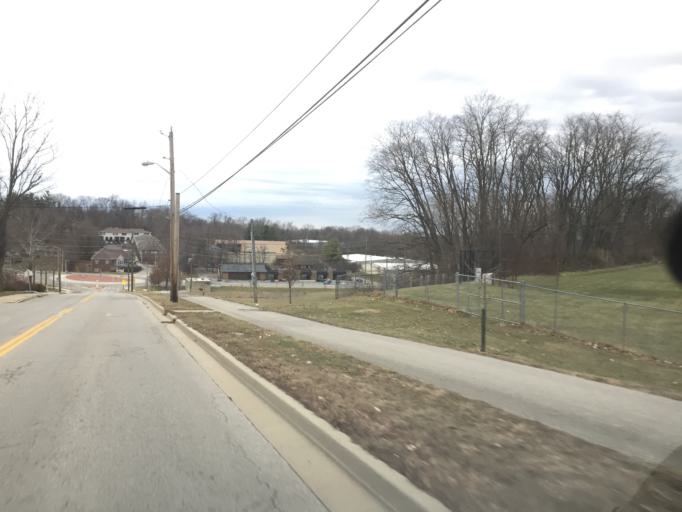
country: US
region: Indiana
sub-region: Monroe County
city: Bloomington
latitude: 39.1771
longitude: -86.5471
